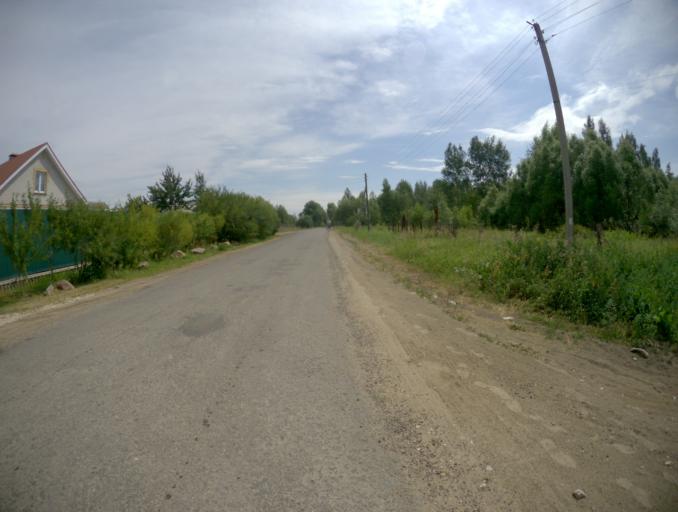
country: RU
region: Vladimir
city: Raduzhnyy
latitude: 56.0248
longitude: 40.3148
